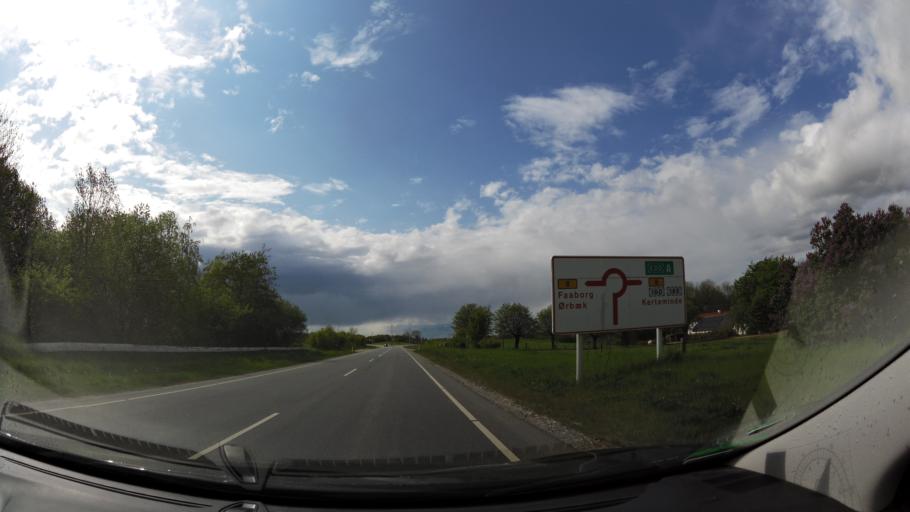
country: DK
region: South Denmark
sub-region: Nyborg Kommune
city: Nyborg
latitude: 55.3205
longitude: 10.7376
